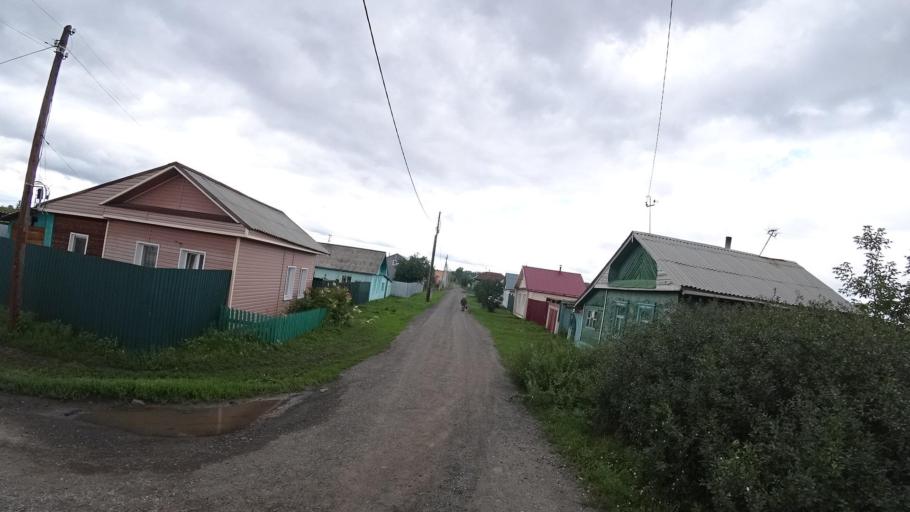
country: RU
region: Sverdlovsk
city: Kamyshlov
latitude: 56.8522
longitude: 62.6890
